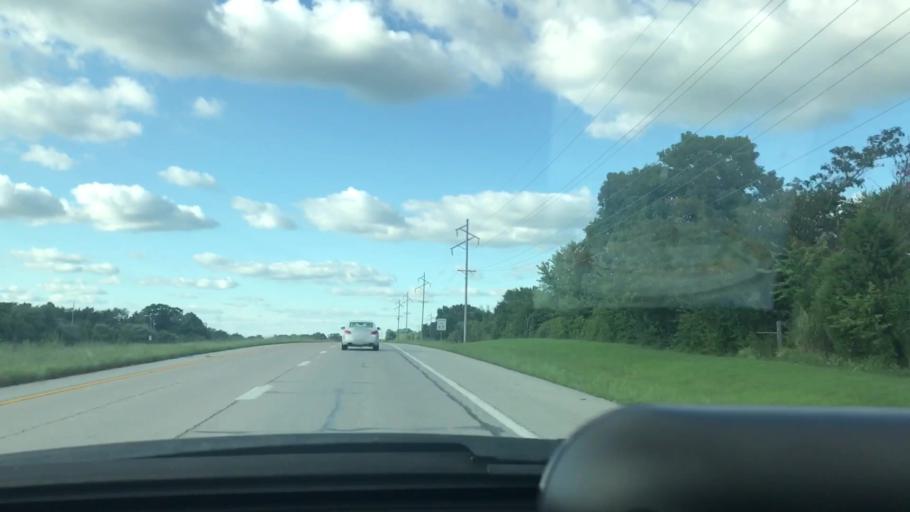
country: US
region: Missouri
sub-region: Pettis County
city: Sedalia
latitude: 38.6266
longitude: -93.2672
